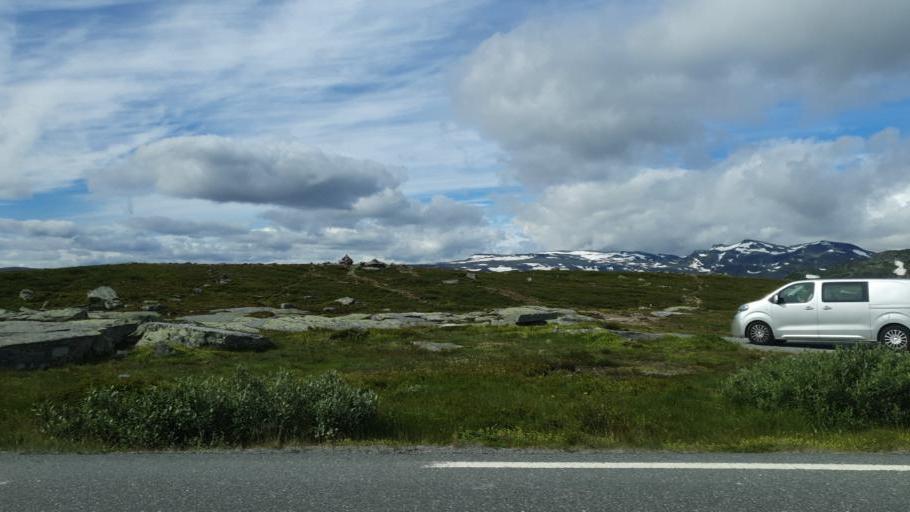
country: NO
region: Oppland
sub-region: Vestre Slidre
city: Slidre
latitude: 61.2836
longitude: 8.8300
